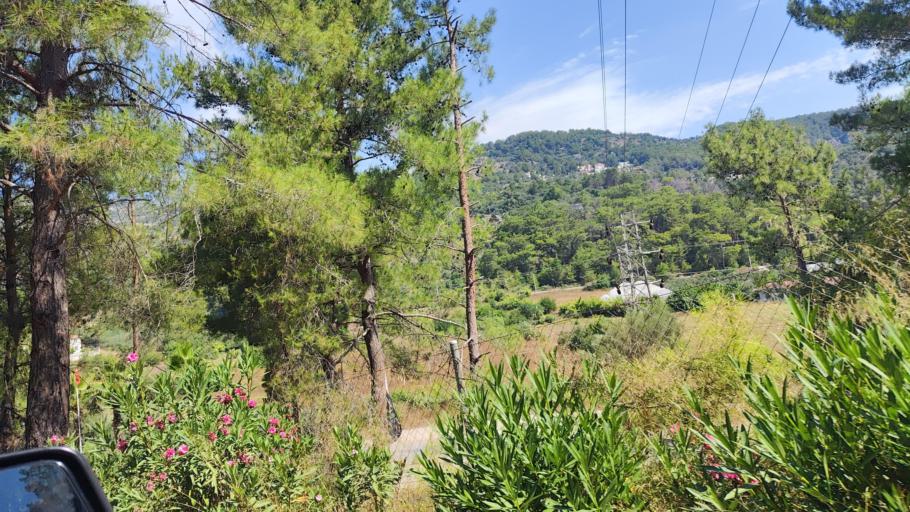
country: TR
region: Mugla
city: Sarigerme
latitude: 36.7072
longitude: 28.6952
